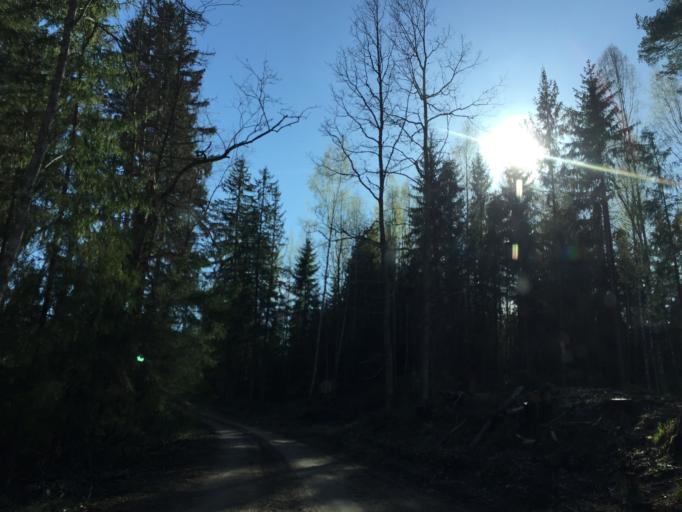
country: EE
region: Valgamaa
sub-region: Valga linn
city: Valga
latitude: 57.7748
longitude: 26.2272
